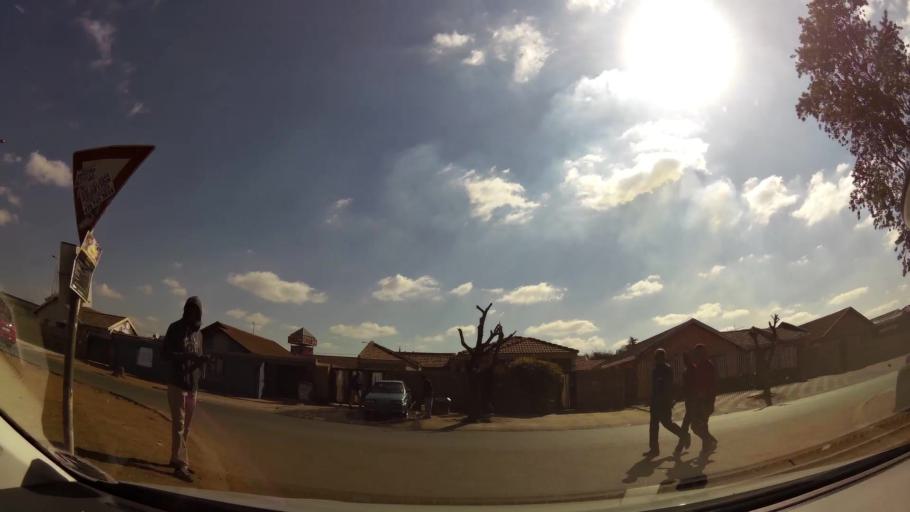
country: ZA
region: Gauteng
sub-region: City of Johannesburg Metropolitan Municipality
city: Roodepoort
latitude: -26.2111
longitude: 27.8710
